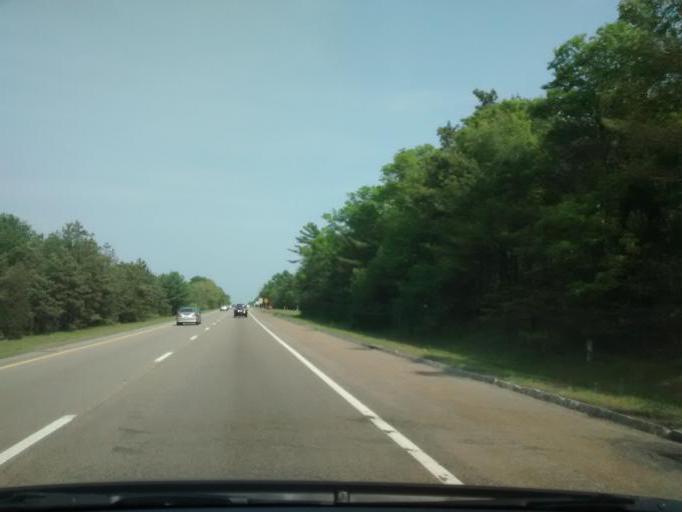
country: US
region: Massachusetts
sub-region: Plymouth County
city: Wareham Center
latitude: 41.7835
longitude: -70.7317
